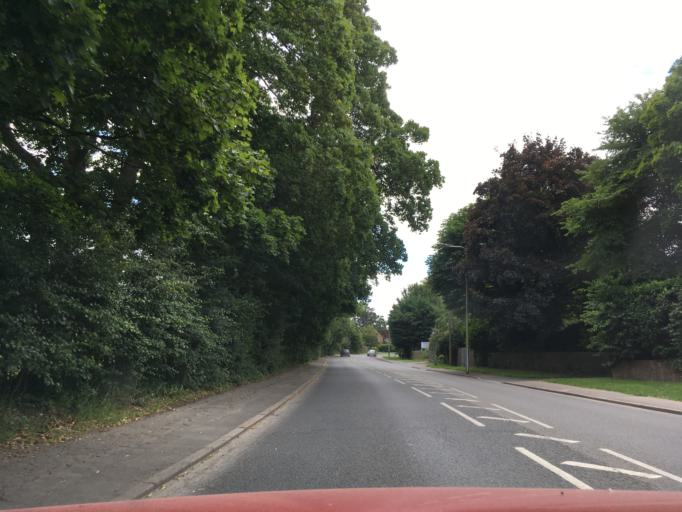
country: GB
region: England
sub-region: West Berkshire
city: Newbury
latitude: 51.4125
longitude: -1.3319
